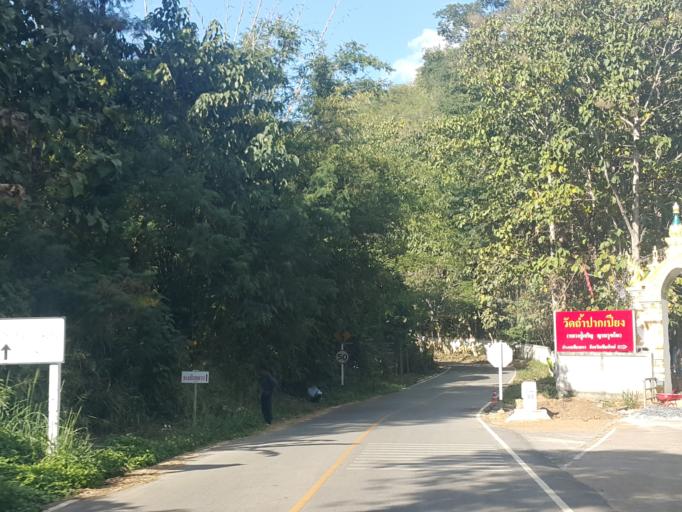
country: TH
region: Chiang Mai
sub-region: Amphoe Chiang Dao
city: Chiang Dao
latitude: 19.4031
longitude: 98.9282
